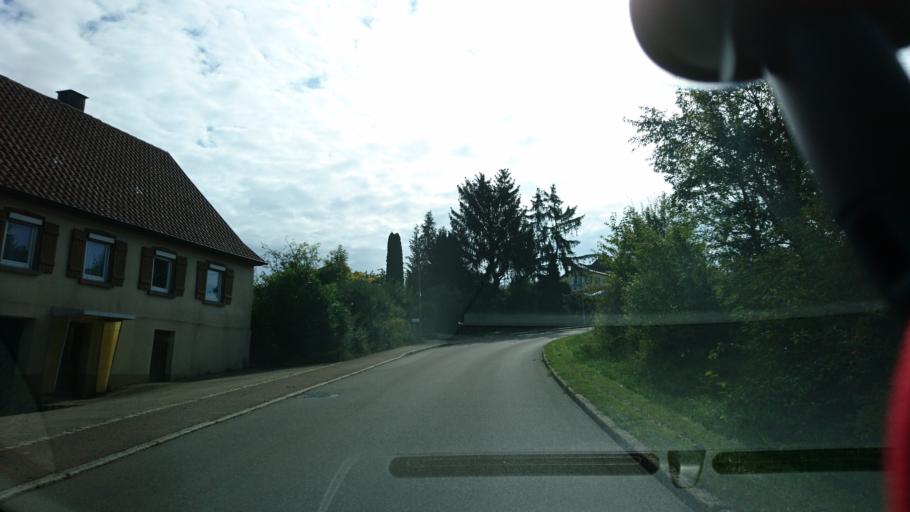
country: DE
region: Baden-Wuerttemberg
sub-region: Regierungsbezirk Stuttgart
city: Mainhardt
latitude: 49.1018
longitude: 9.5731
